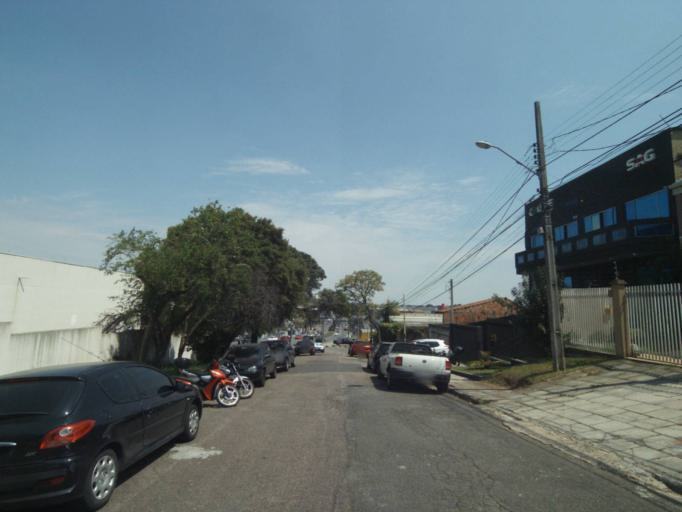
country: BR
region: Parana
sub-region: Curitiba
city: Curitiba
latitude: -25.4783
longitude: -49.3138
